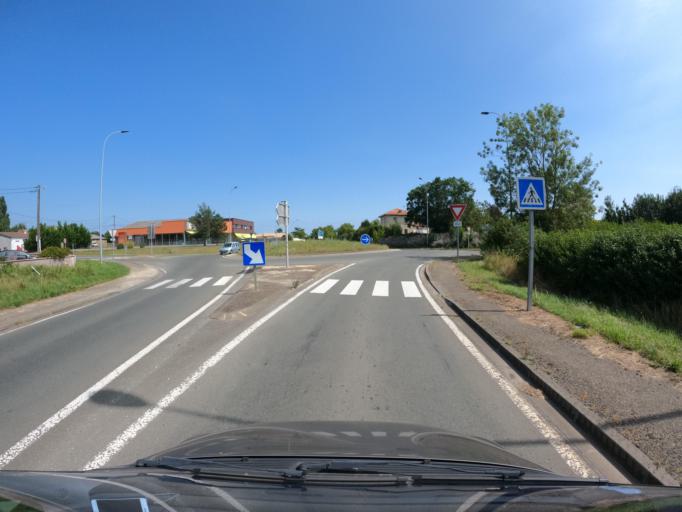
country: FR
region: Poitou-Charentes
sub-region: Departement des Deux-Sevres
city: Bessines
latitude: 46.2967
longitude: -0.5001
